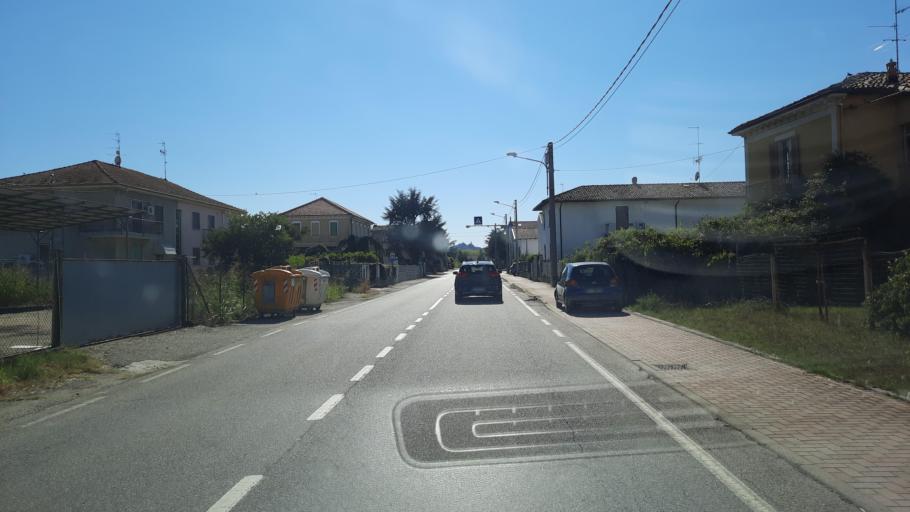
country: IT
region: Piedmont
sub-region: Provincia di Alessandria
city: Conzano
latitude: 45.0505
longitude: 8.4476
